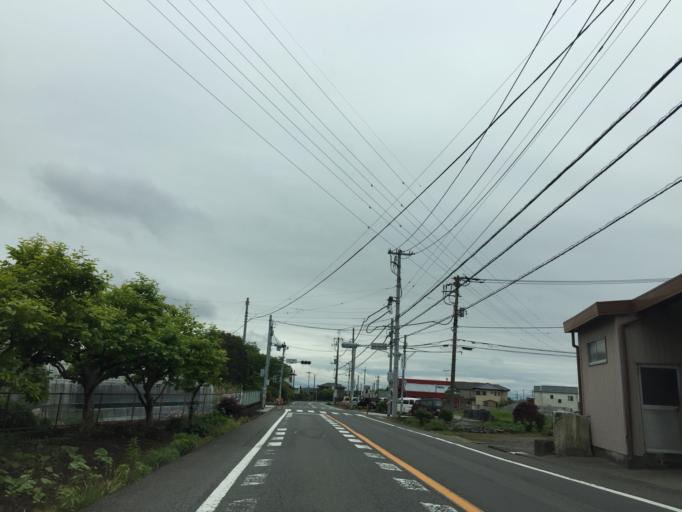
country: JP
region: Shizuoka
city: Mishima
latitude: 35.1884
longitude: 138.9214
